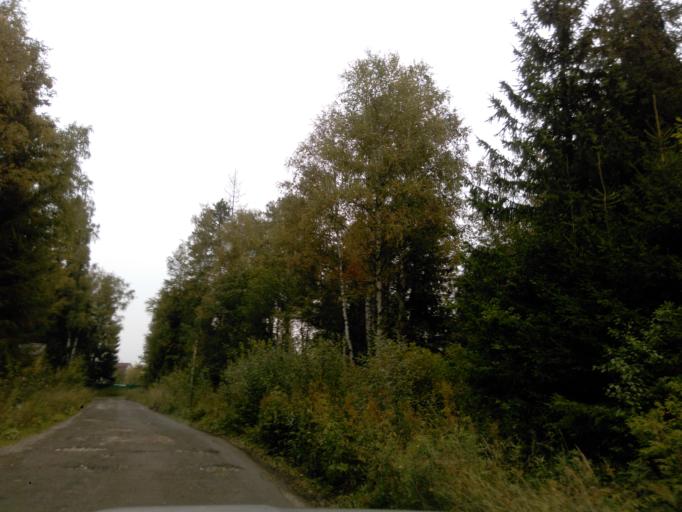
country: RU
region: Moskovskaya
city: Mendeleyevo
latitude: 56.0904
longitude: 37.2639
